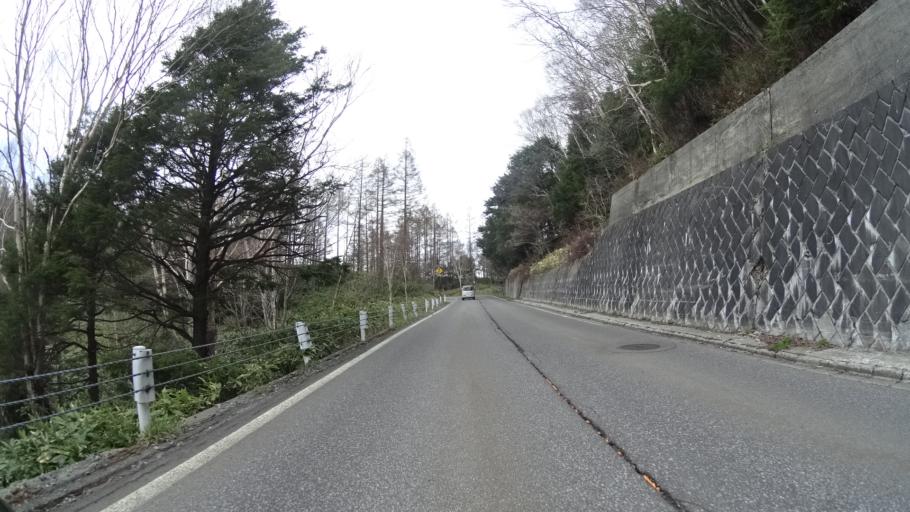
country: JP
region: Nagano
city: Nakano
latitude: 36.7040
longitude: 138.4911
